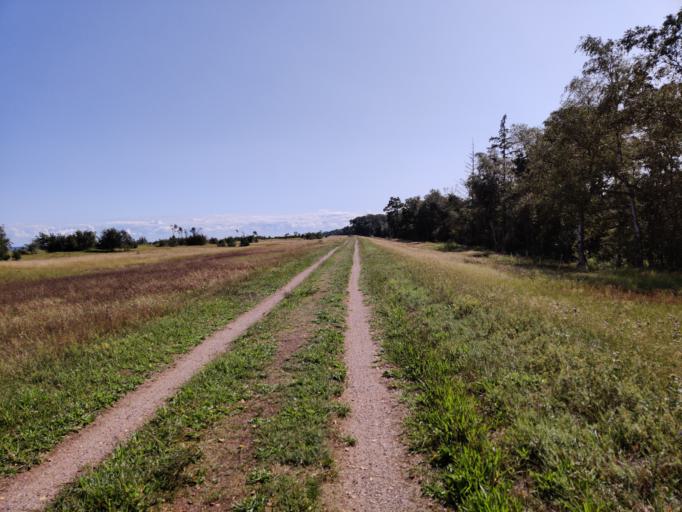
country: DK
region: Zealand
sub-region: Guldborgsund Kommune
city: Nykobing Falster
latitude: 54.6270
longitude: 11.9621
